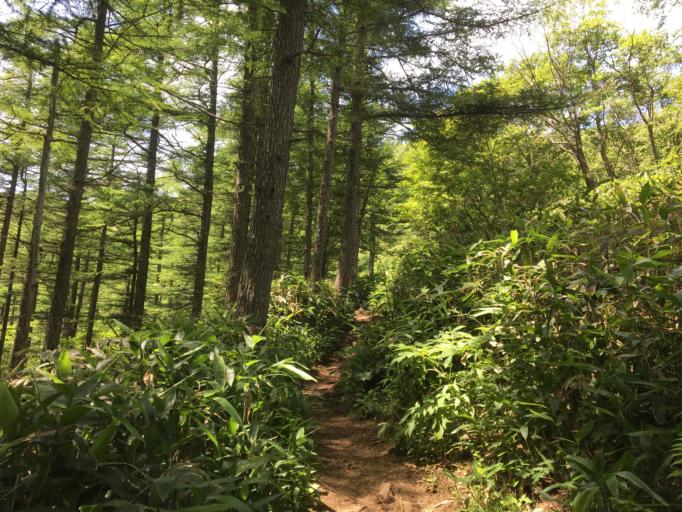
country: JP
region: Nagano
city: Ueda
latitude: 36.4321
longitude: 138.3934
